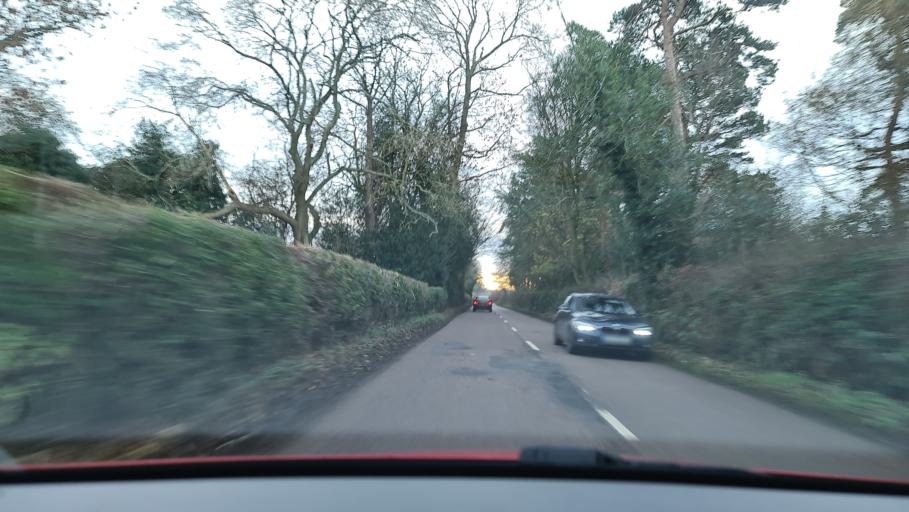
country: GB
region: England
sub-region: Buckinghamshire
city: Great Missenden
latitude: 51.7014
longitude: -0.6701
